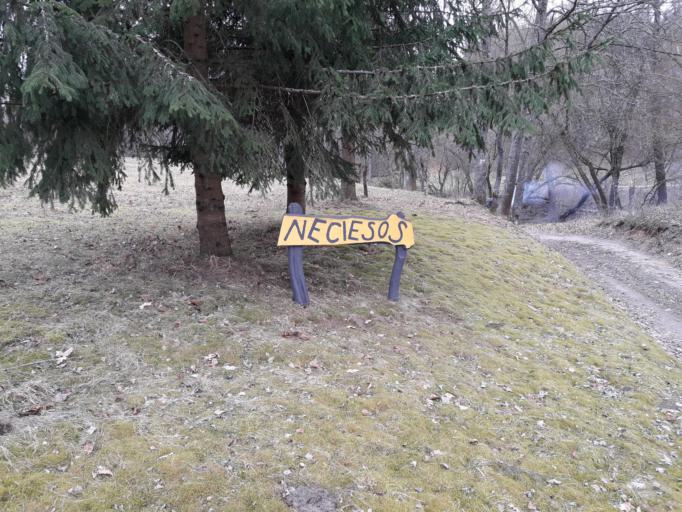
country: LT
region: Alytaus apskritis
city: Druskininkai
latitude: 54.1853
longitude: 24.0826
